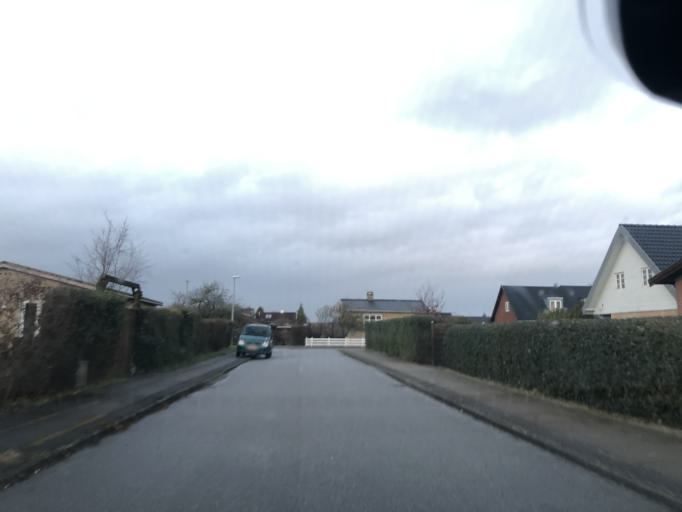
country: DK
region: Capital Region
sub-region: Tarnby Kommune
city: Tarnby
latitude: 55.6133
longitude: 12.6037
